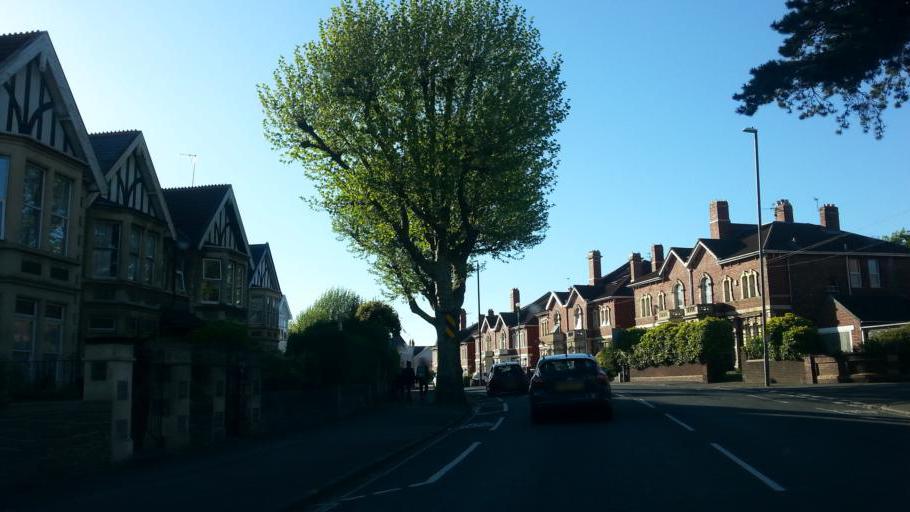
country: GB
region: England
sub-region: Bath and North East Somerset
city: Whitchurch
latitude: 51.4372
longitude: -2.5697
